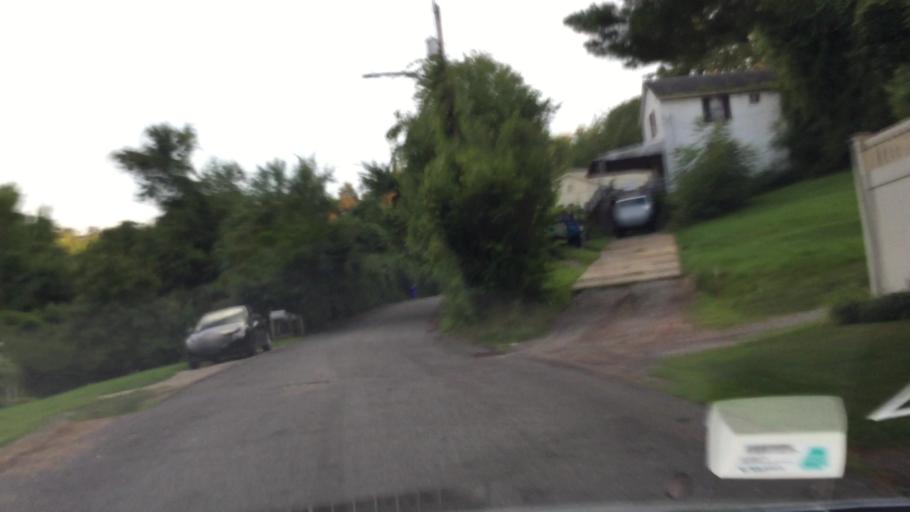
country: US
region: Pennsylvania
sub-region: Allegheny County
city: Imperial
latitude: 40.4336
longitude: -80.2708
